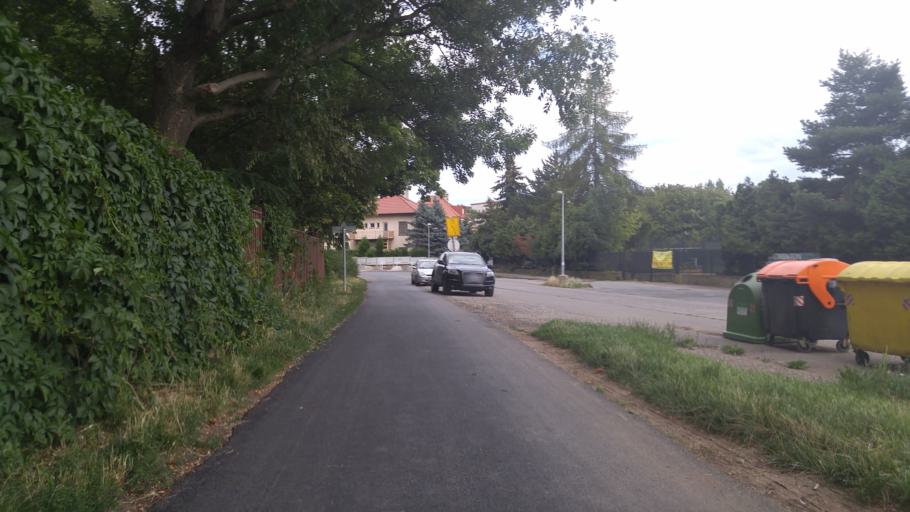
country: CZ
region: Central Bohemia
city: Horomerice
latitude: 50.0987
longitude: 14.3413
